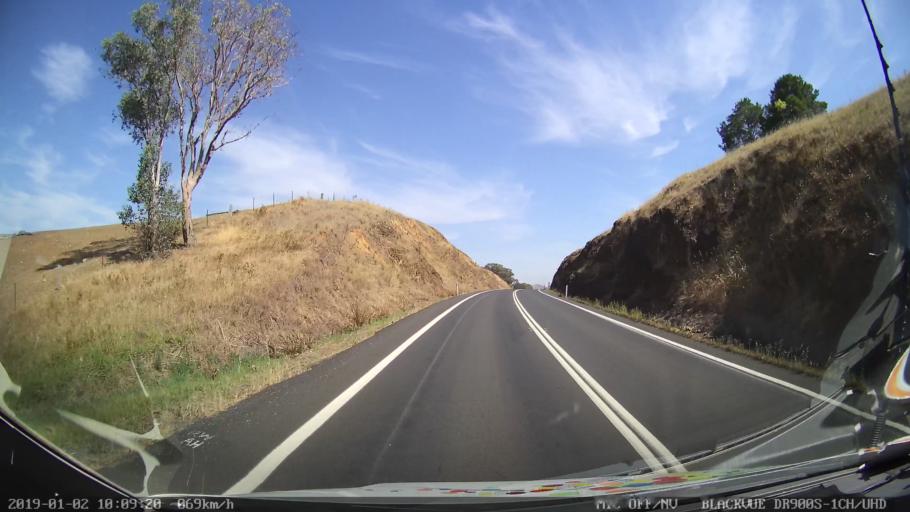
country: AU
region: New South Wales
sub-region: Gundagai
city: Gundagai
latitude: -35.1178
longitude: 148.0993
